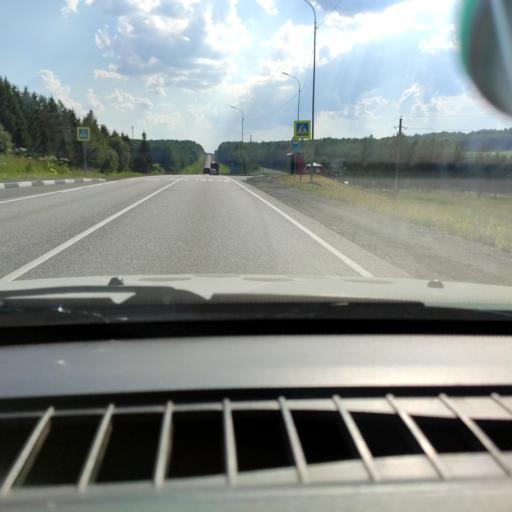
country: RU
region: Perm
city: Pavlovskiy
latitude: 57.8917
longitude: 54.9373
